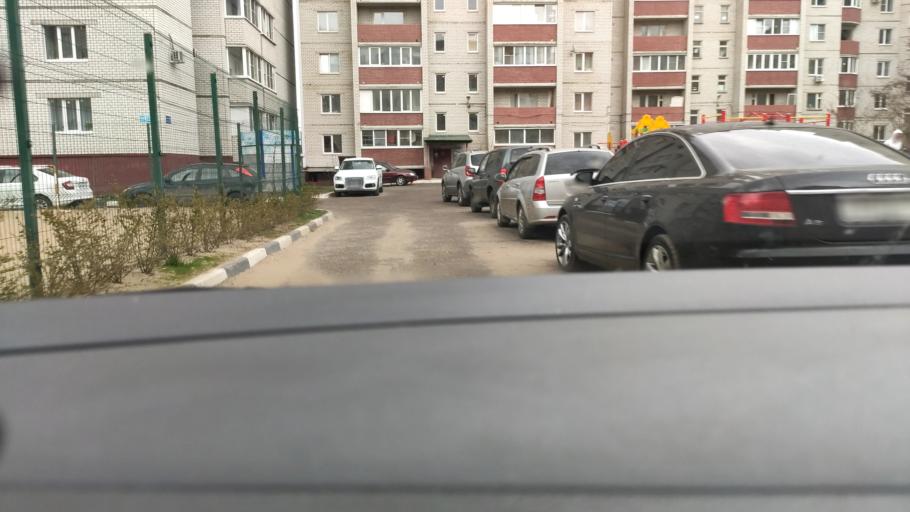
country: RU
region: Voronezj
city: Podgornoye
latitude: 51.7337
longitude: 39.1957
